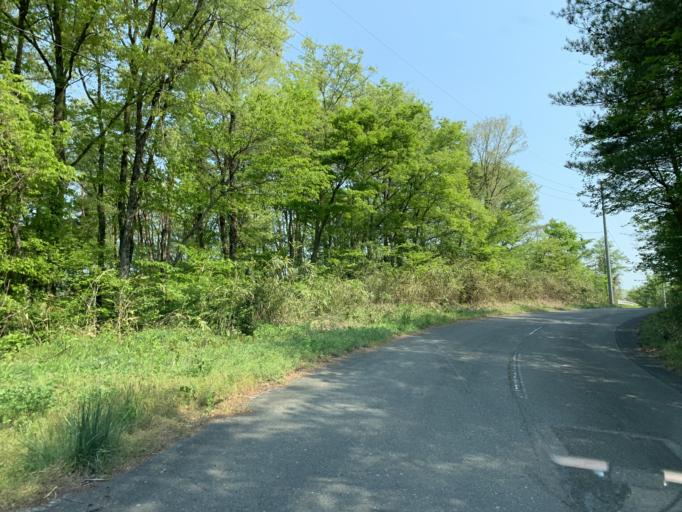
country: JP
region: Iwate
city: Ichinoseki
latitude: 38.8884
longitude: 141.0651
